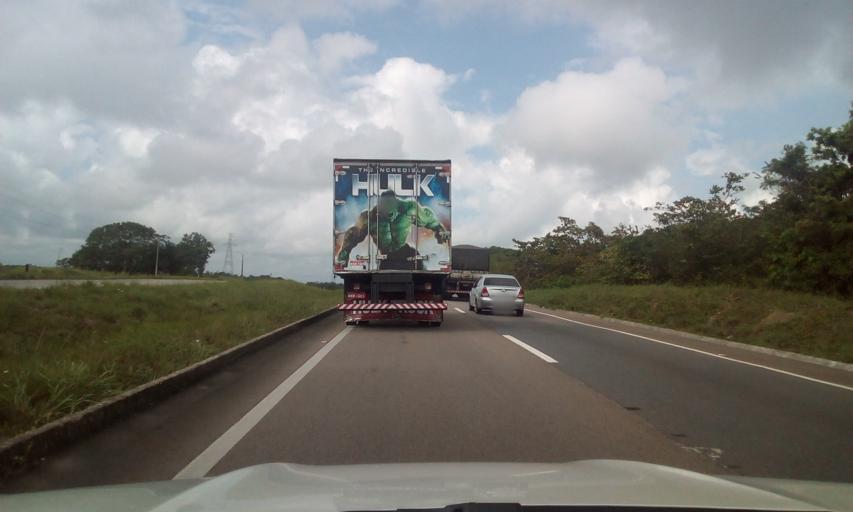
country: BR
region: Paraiba
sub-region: Conde
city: Conde
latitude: -7.3047
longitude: -34.9414
